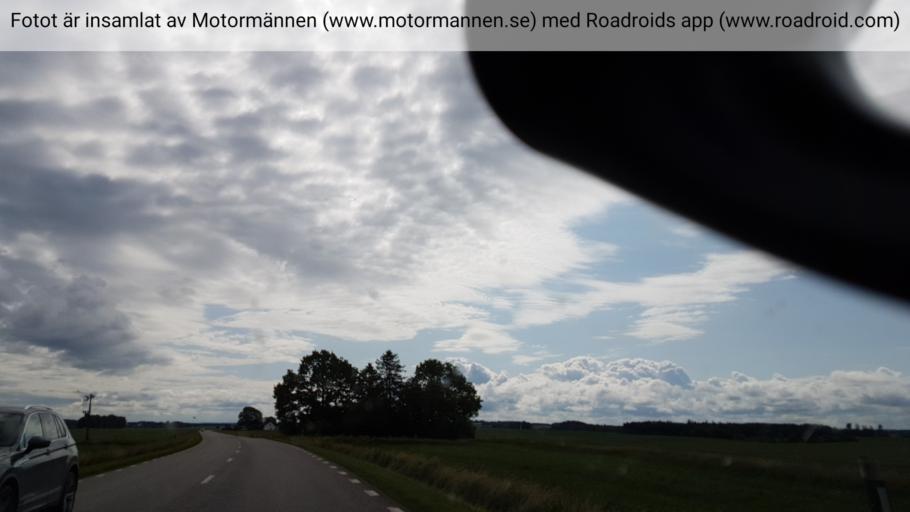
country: SE
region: Vaestra Goetaland
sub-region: Vara Kommun
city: Kvanum
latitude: 58.2360
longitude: 13.1171
